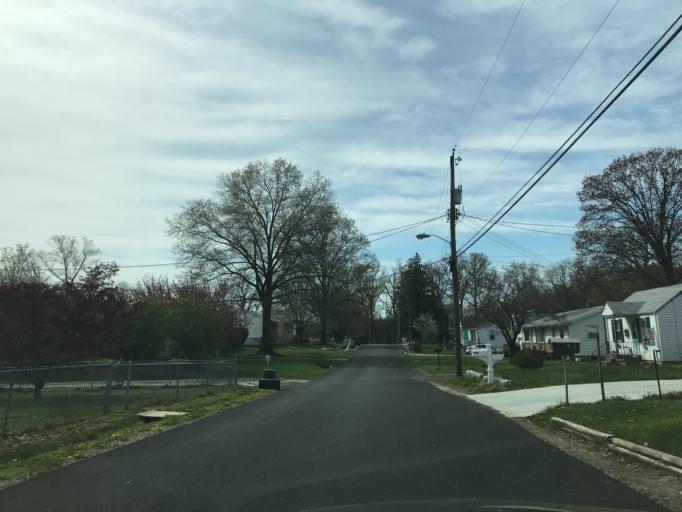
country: US
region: Maryland
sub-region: Baltimore County
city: Middle River
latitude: 39.3064
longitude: -76.4314
